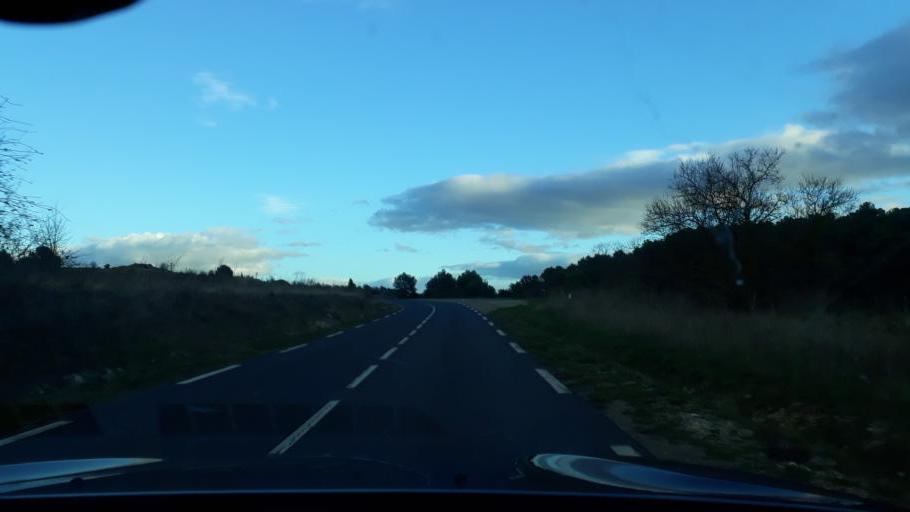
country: FR
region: Languedoc-Roussillon
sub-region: Departement de l'Herault
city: Nissan-lez-Enserune
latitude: 43.2851
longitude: 3.1398
